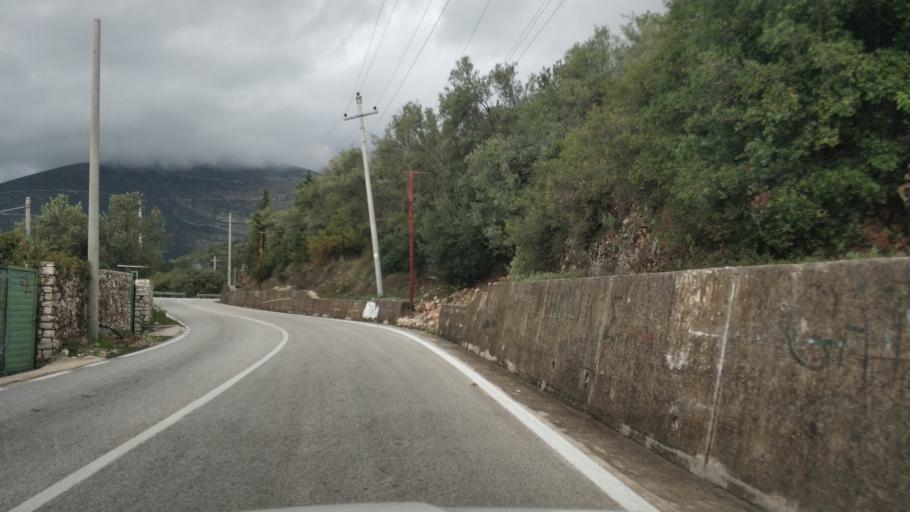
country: AL
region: Vlore
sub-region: Rrethi i Vlores
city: Vranisht
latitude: 40.1641
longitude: 19.6210
